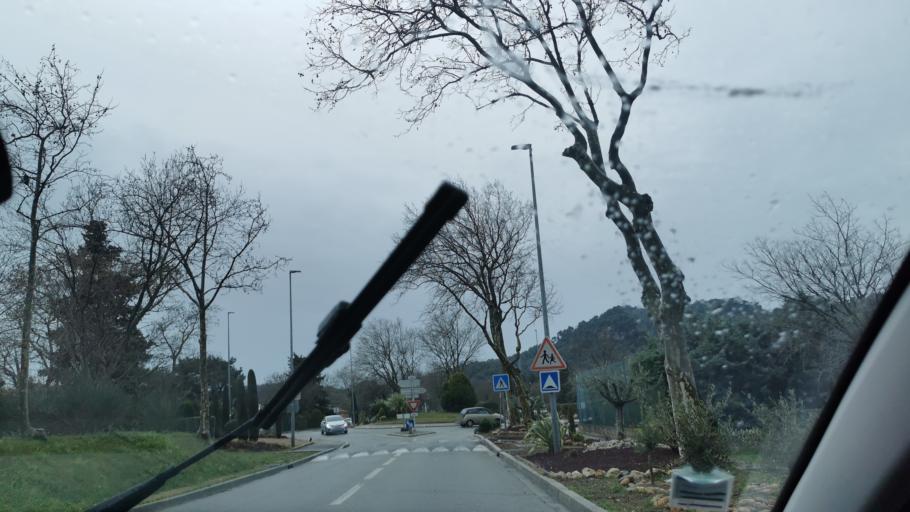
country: FR
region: Provence-Alpes-Cote d'Azur
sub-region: Departement des Bouches-du-Rhone
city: Lamanon
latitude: 43.7002
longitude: 5.0896
